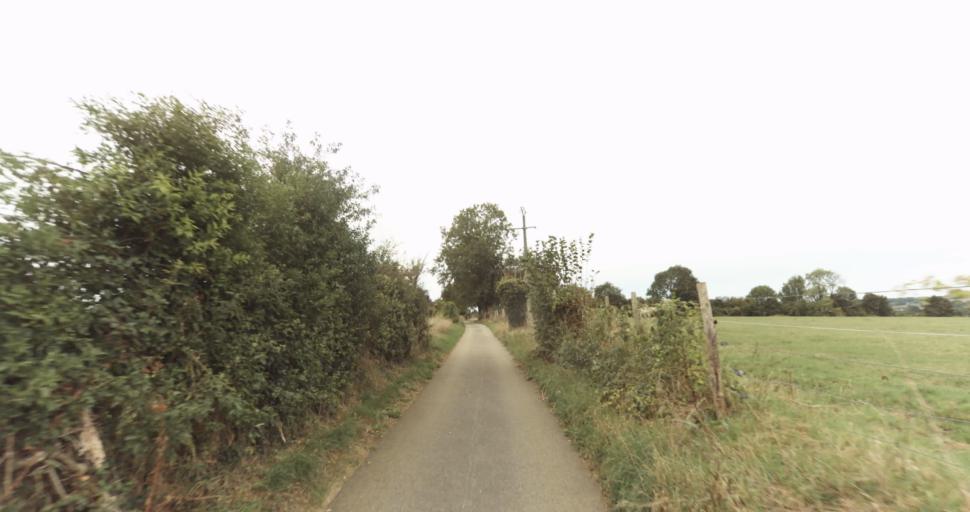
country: FR
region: Lower Normandy
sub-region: Departement de l'Orne
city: Gace
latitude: 48.7624
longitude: 0.3232
